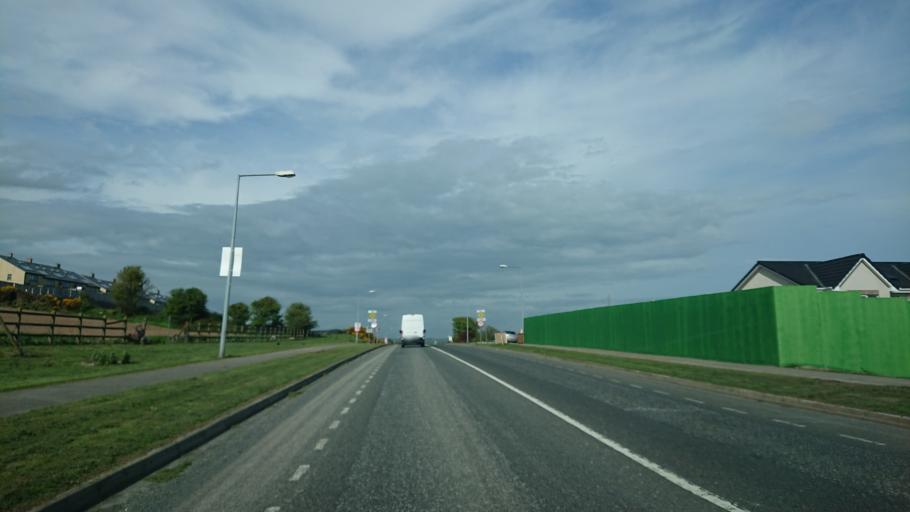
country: IE
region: Munster
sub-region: Waterford
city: Waterford
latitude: 52.2588
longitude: -7.1532
